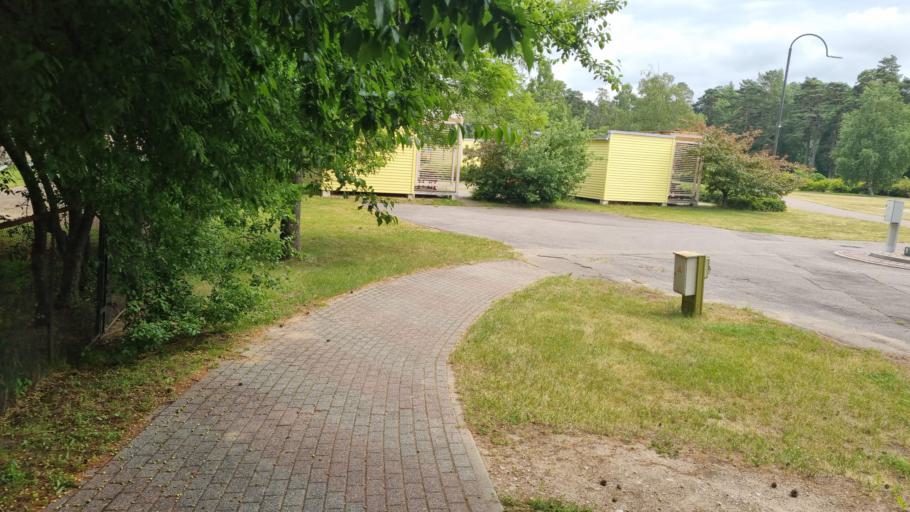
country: LV
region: Ventspils
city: Ventspils
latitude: 57.3850
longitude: 21.5335
